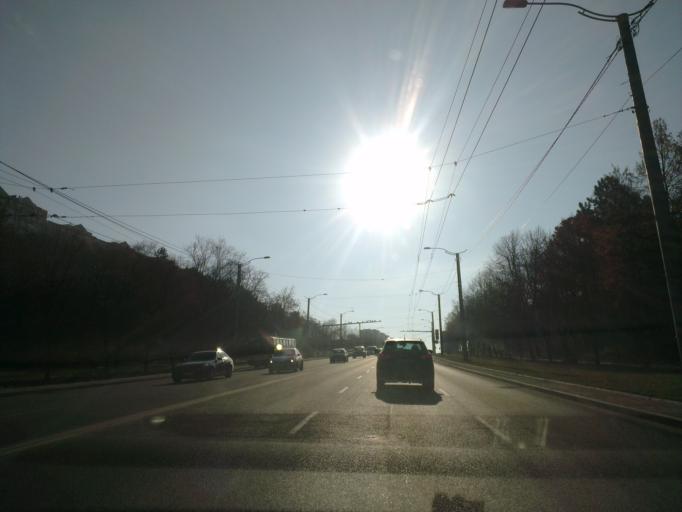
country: MD
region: Chisinau
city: Chisinau
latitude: 47.0409
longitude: 28.8778
